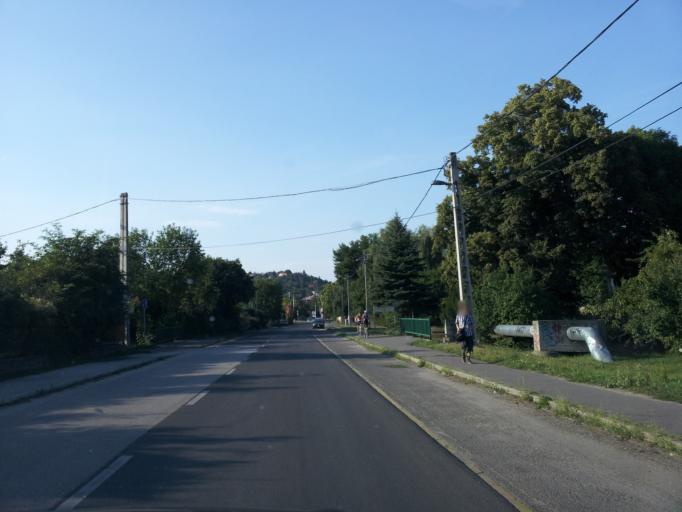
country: HU
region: Pest
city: Szentendre
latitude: 47.6761
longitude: 19.0801
